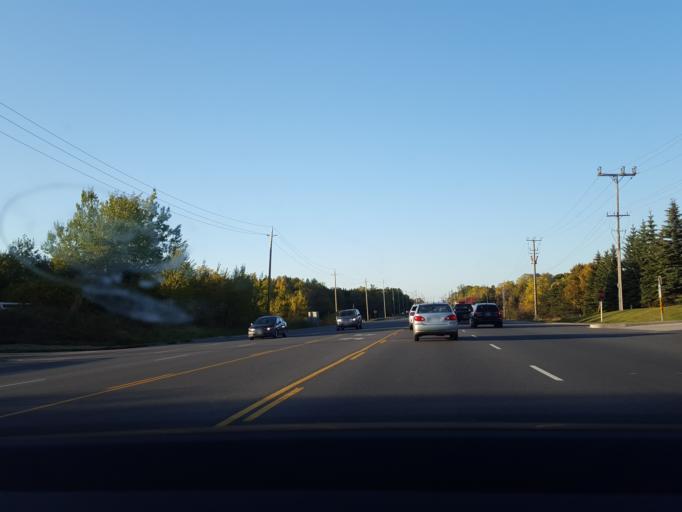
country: CA
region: Ontario
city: Newmarket
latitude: 44.0192
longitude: -79.4721
